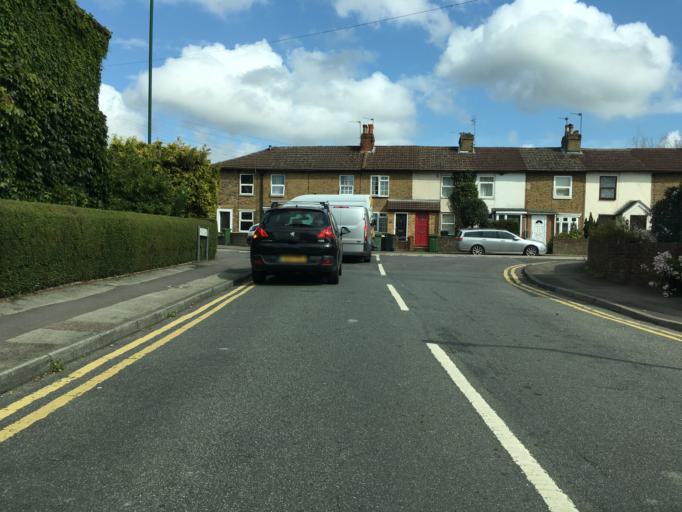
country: GB
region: England
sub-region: Kent
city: Maidstone
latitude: 51.2460
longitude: 0.5239
